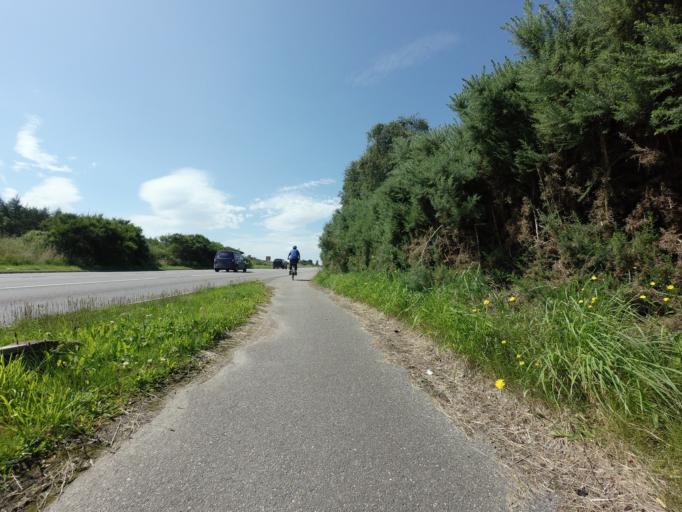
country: GB
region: Scotland
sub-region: Highland
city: Conon Bridge
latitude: 57.5397
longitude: -4.3504
